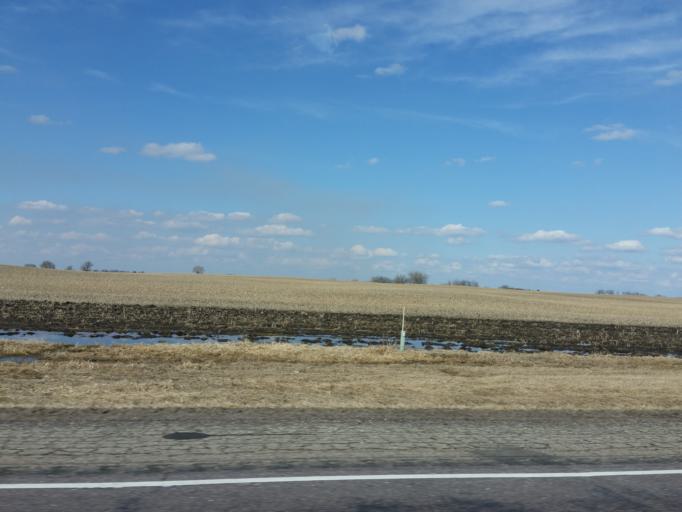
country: US
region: Minnesota
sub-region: Lac qui Parle County
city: Madison
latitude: 44.9358
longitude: -96.2827
